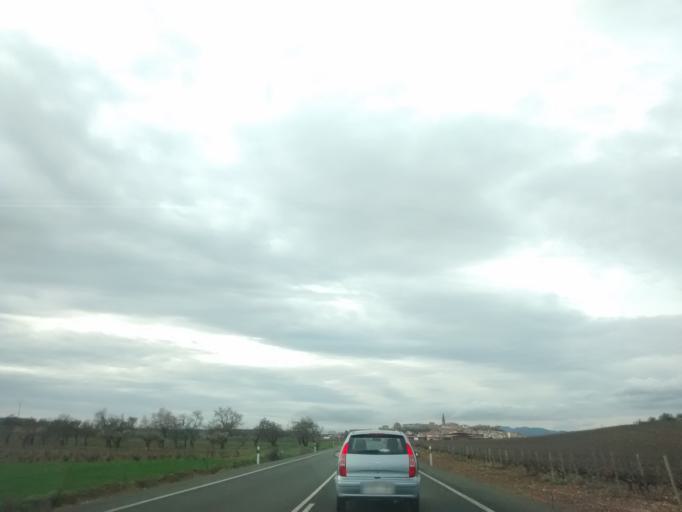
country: ES
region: La Rioja
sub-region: Provincia de La Rioja
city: Briones
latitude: 42.5324
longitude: -2.7649
